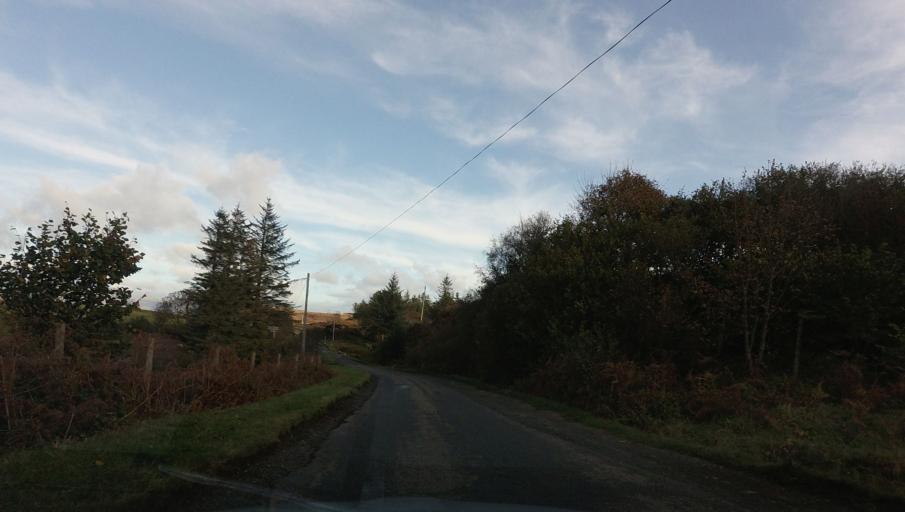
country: GB
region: Scotland
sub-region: Argyll and Bute
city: Isle Of Mull
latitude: 56.3307
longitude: -6.1884
